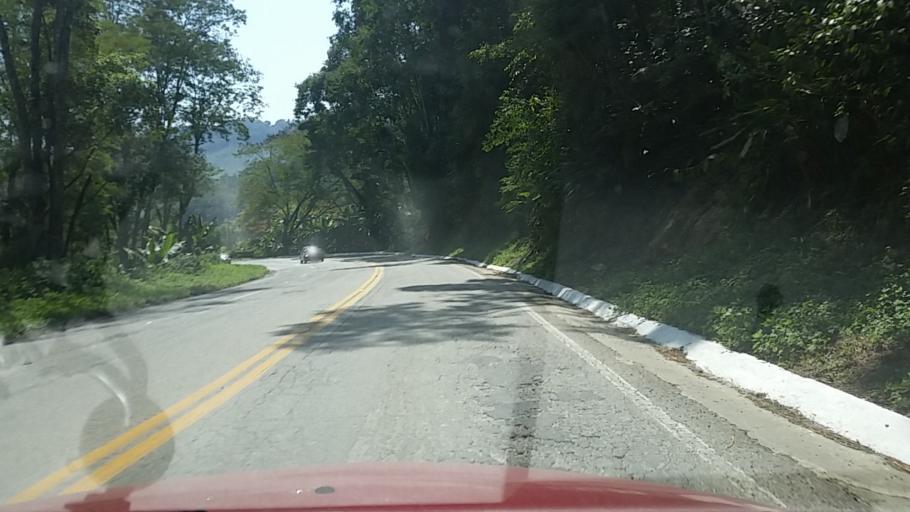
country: BR
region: Sao Paulo
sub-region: Miracatu
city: Miracatu
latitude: -24.3460
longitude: -47.4981
